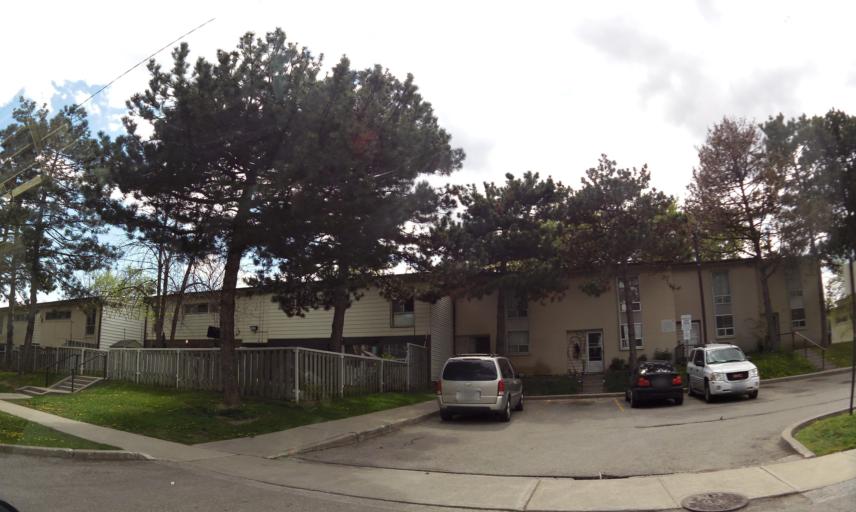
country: CA
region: Ontario
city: Etobicoke
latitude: 43.6510
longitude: -79.5695
